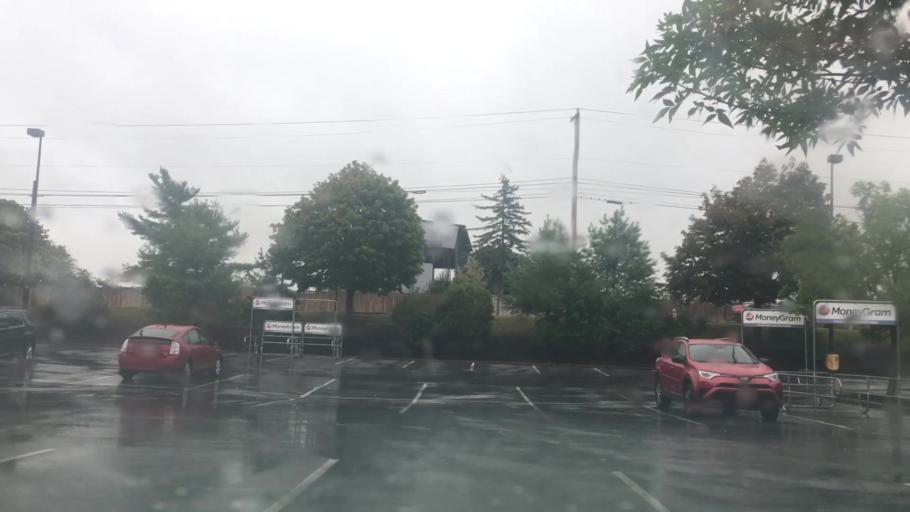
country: US
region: Maine
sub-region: Penobscot County
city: Bangor
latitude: 44.7936
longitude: -68.7762
